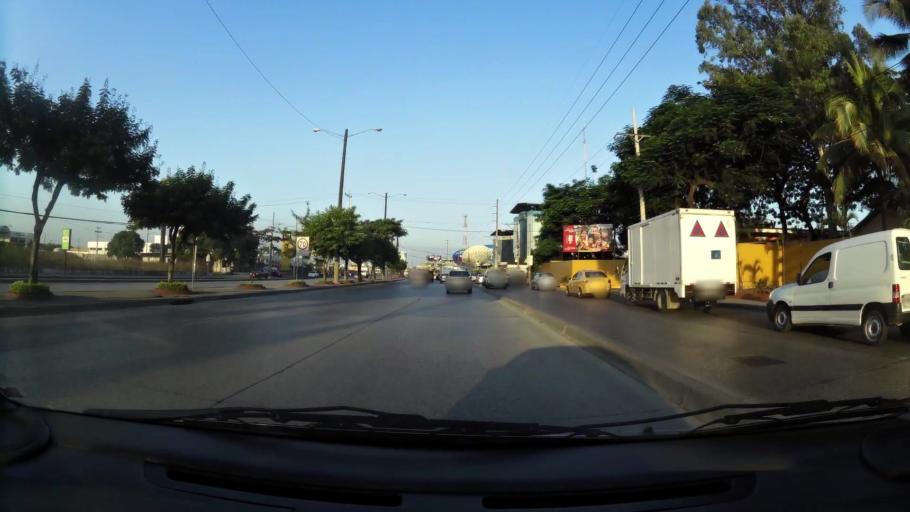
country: EC
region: Guayas
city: Guayaquil
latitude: -2.1476
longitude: -79.9101
